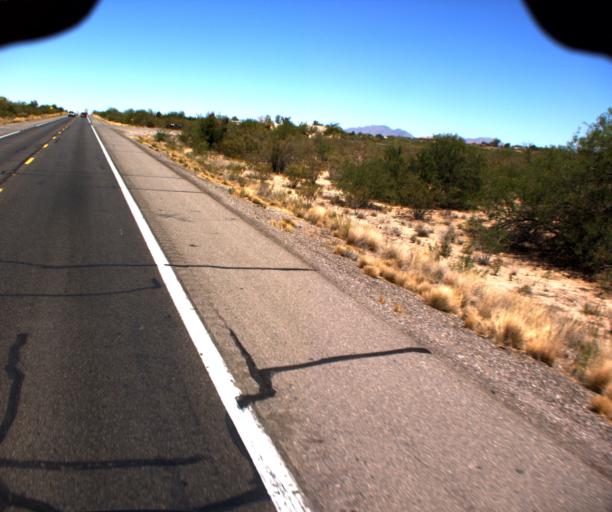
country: US
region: Arizona
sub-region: Maricopa County
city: Wickenburg
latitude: 34.0348
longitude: -112.8233
